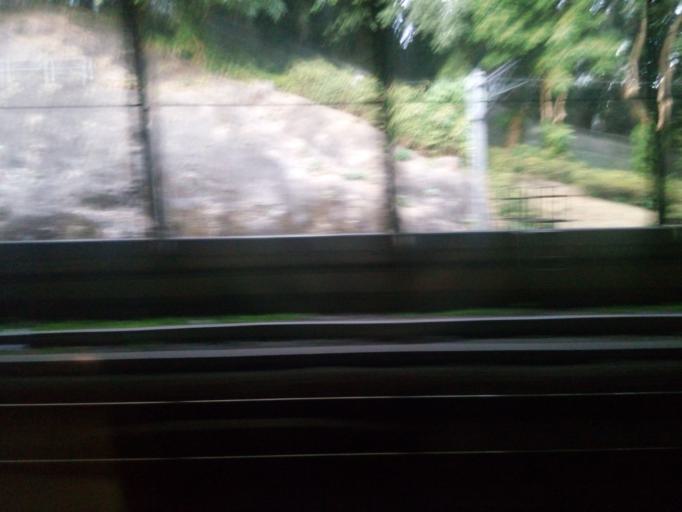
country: HK
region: Tai Po
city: Tai Po
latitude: 22.4446
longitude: 114.1689
